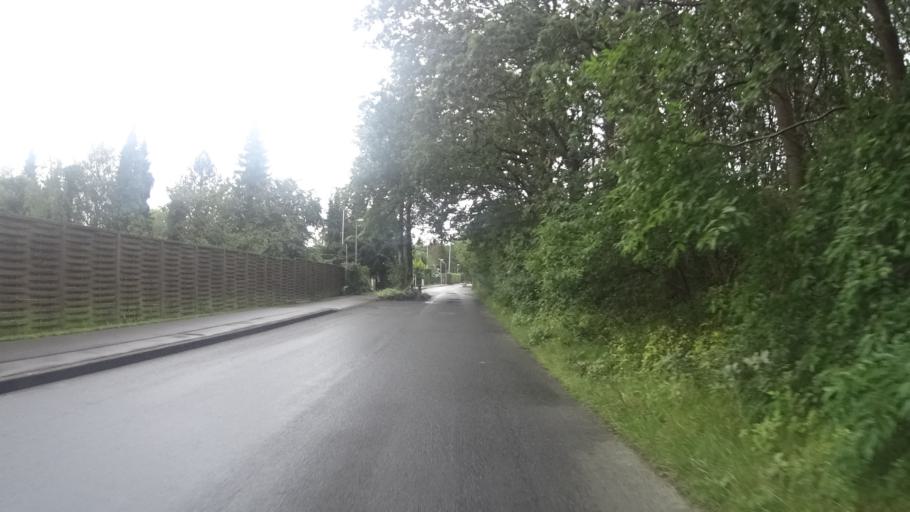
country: DE
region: Schleswig-Holstein
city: Kiebitzreihe
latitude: 53.7831
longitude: 9.6256
